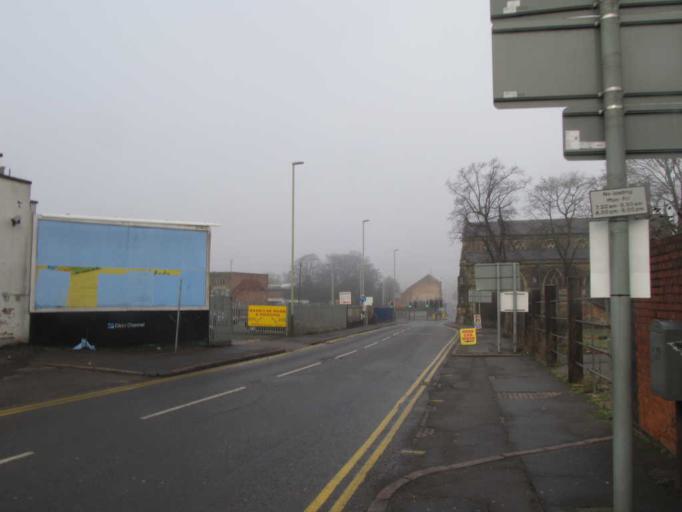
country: GB
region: England
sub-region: City of Leicester
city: Leicester
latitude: 52.6375
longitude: -1.1400
